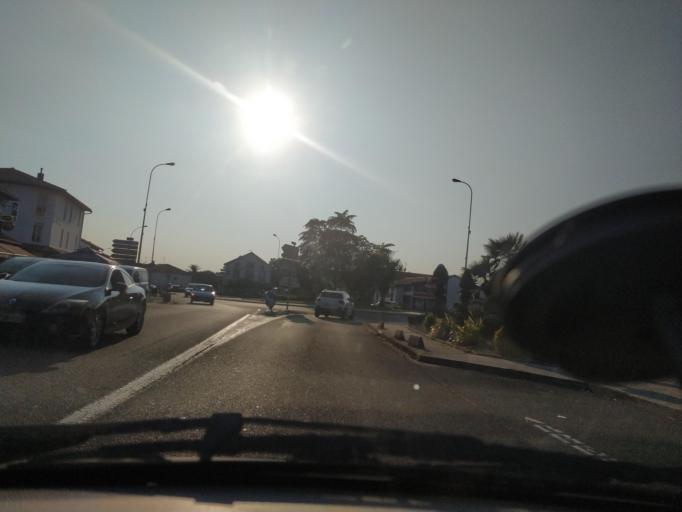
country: FR
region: Aquitaine
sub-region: Departement des Landes
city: Saint-Geours-de-Maremne
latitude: 43.6876
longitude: -1.2288
